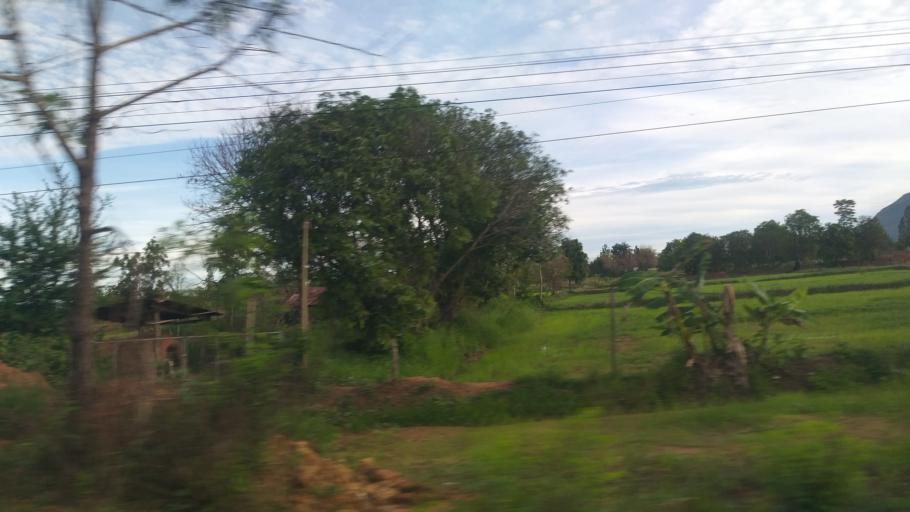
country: TH
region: Chaiyaphum
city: Phu Khiao
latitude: 16.3266
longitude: 102.2131
